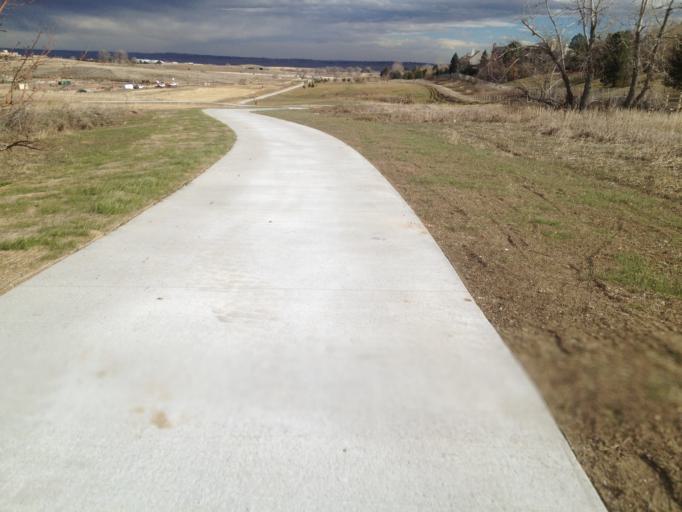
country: US
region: Colorado
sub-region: Boulder County
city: Superior
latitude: 39.9471
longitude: -105.1630
